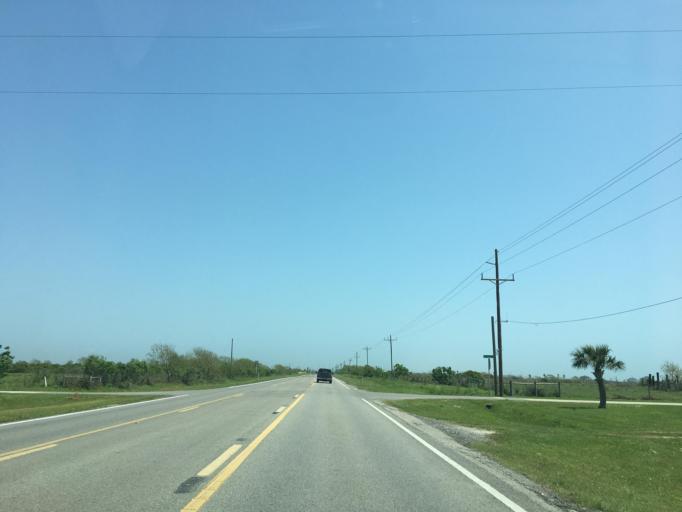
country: US
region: Texas
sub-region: Galveston County
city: Bolivar Peninsula
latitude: 29.4306
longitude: -94.6863
